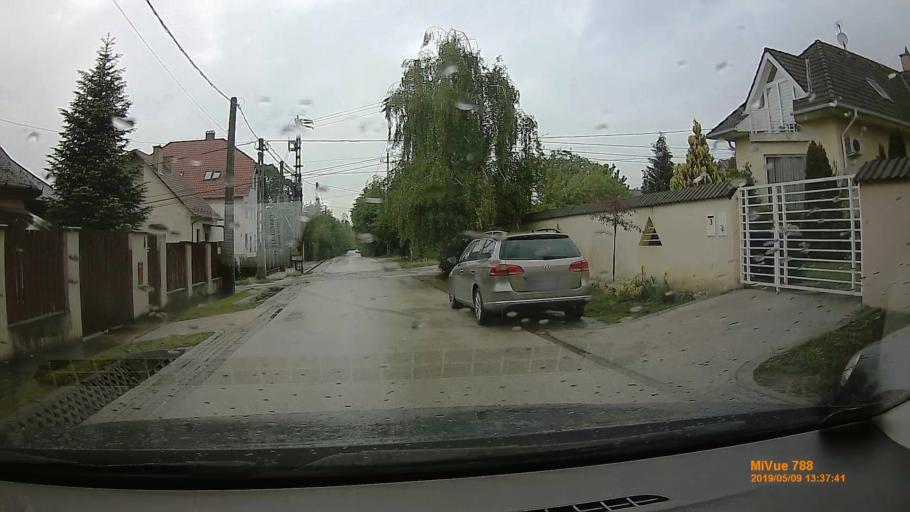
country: HU
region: Budapest
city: Budapest XVI. keruelet
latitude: 47.5289
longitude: 19.1990
